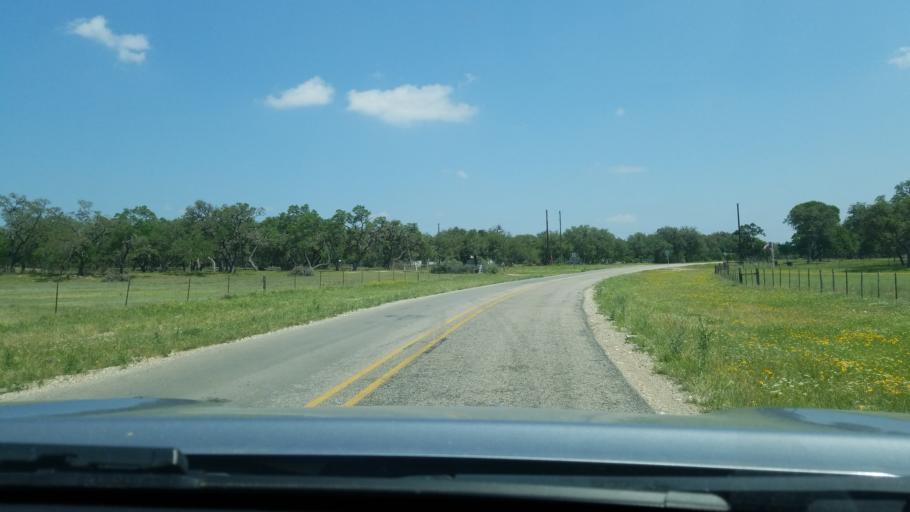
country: US
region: Texas
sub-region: Blanco County
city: Blanco
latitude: 29.9728
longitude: -98.5274
